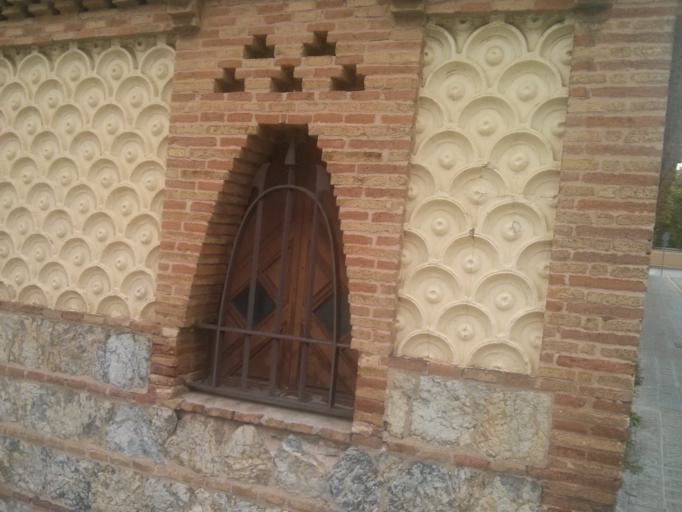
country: ES
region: Catalonia
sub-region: Provincia de Barcelona
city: les Corts
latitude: 41.3894
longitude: 2.1192
